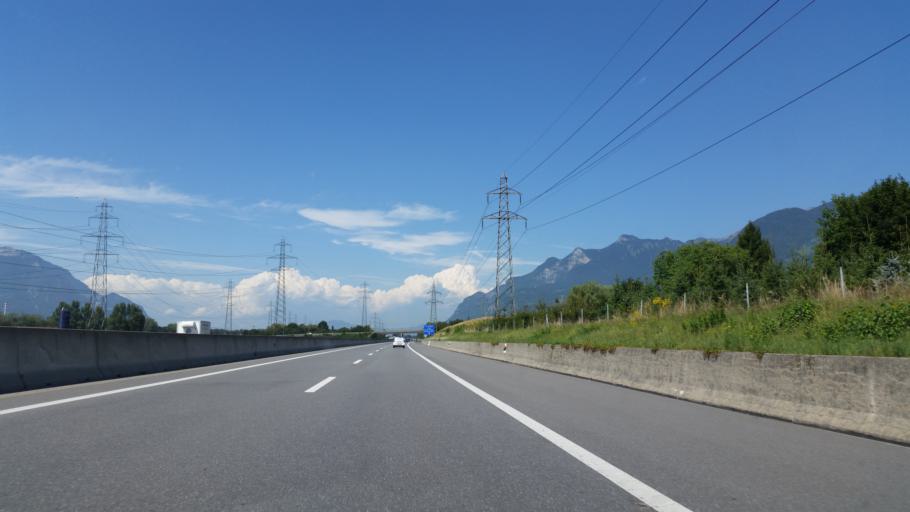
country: CH
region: Valais
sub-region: Monthey District
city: Monthey
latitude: 46.2735
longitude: 6.9716
